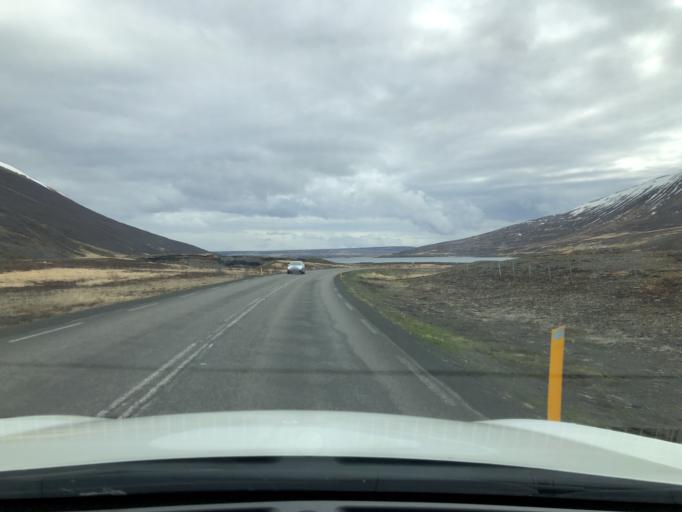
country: IS
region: Northeast
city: Laugar
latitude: 65.7150
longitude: -17.7232
